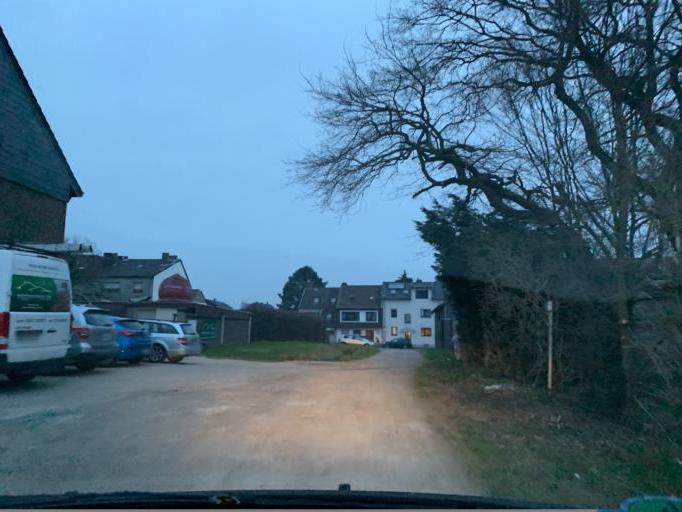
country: DE
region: North Rhine-Westphalia
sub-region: Regierungsbezirk Koln
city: Dueren
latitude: 50.7914
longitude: 6.4393
